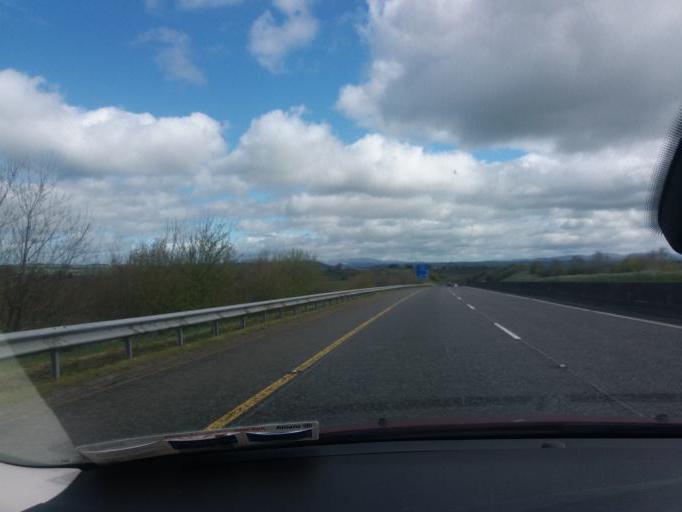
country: IE
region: Munster
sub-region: County Cork
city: Watergrasshill
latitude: 52.0435
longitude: -8.3133
